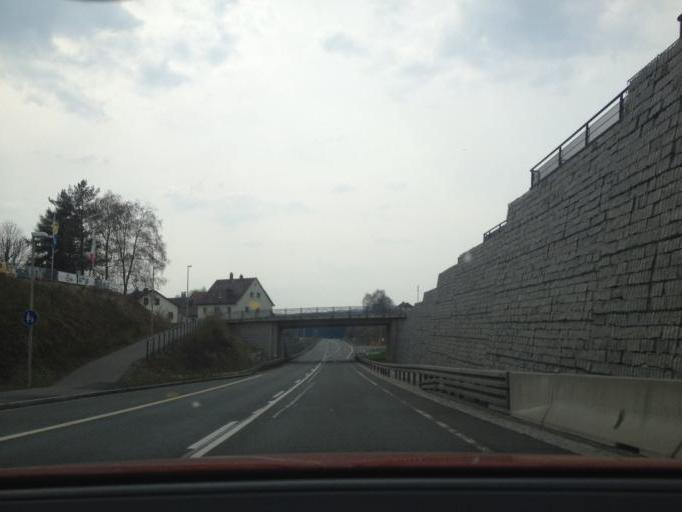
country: DE
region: Bavaria
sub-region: Upper Franconia
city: Bischofsgrun
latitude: 50.0567
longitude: 11.8070
